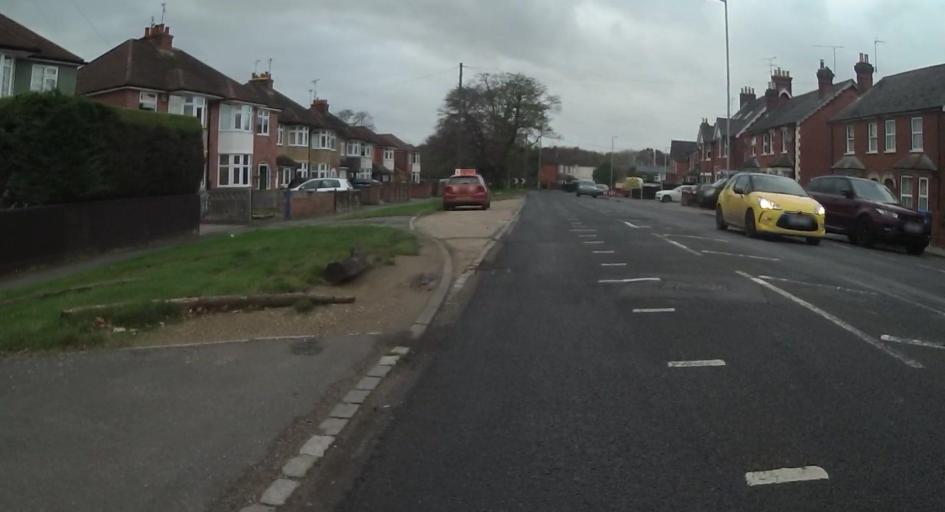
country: GB
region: England
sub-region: Bracknell Forest
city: Sandhurst
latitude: 51.3428
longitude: -0.7821
